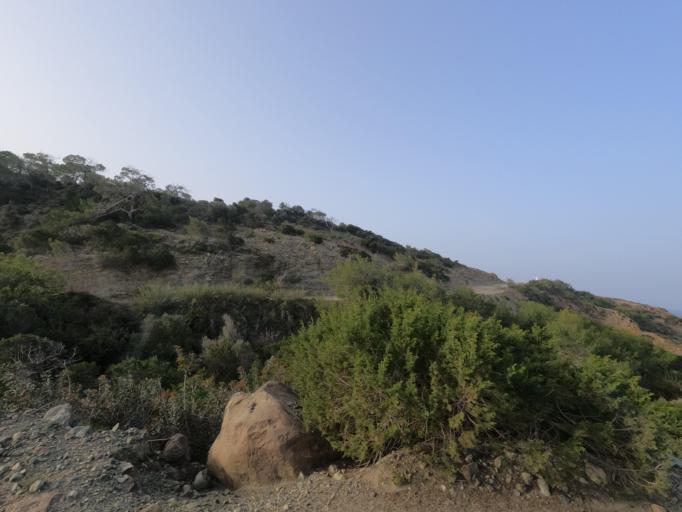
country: CY
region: Pafos
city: Pegeia
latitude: 34.9699
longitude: 32.3135
